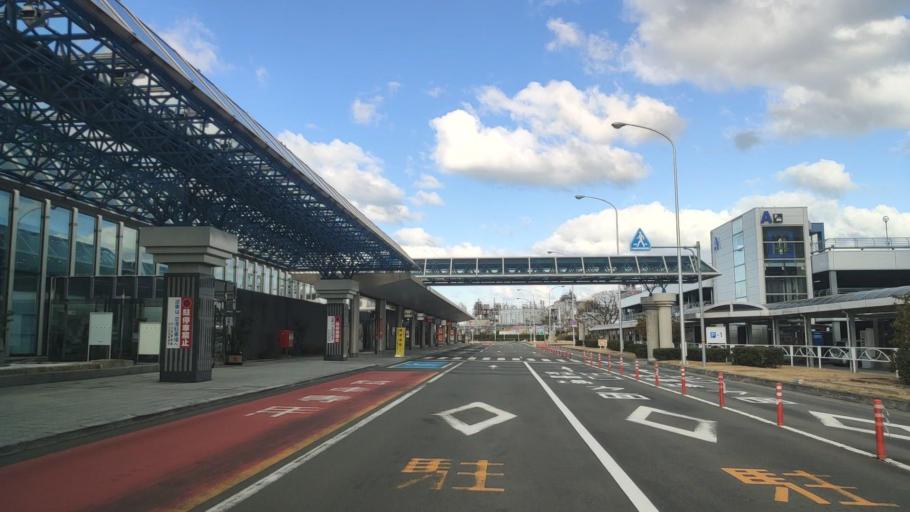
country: JP
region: Ehime
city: Masaki-cho
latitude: 33.8290
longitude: 132.7048
